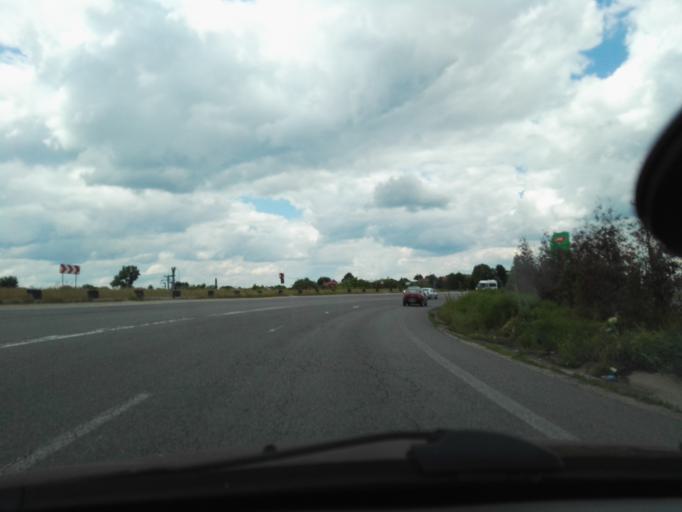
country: RO
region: Giurgiu
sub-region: Comuna Adunatii-Copaceni
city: Adunatii-Copaceni
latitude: 44.2670
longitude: 26.0553
